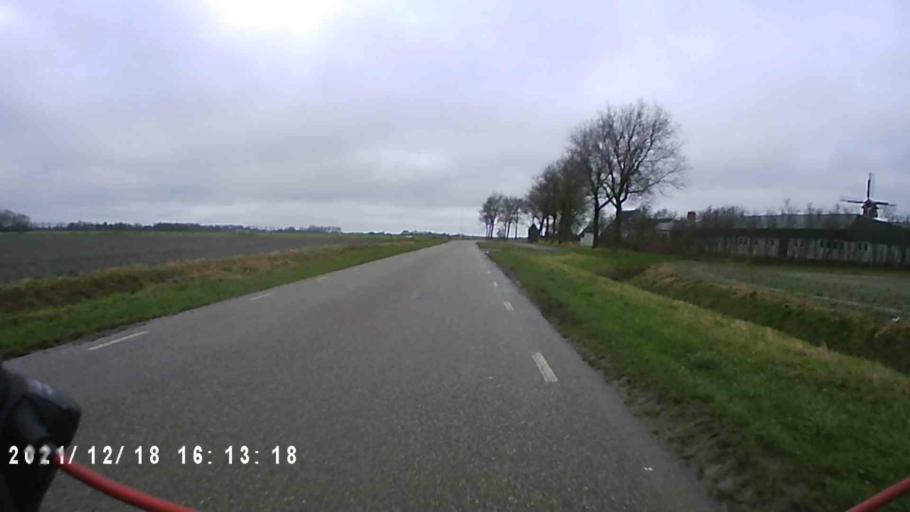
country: NL
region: Friesland
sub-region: Gemeente Dongeradeel
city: Anjum
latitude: 53.3678
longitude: 6.0687
